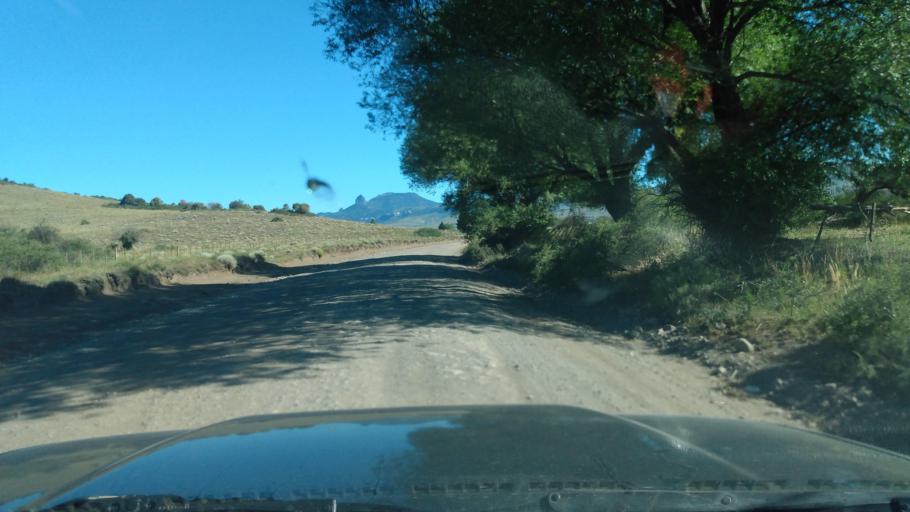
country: AR
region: Neuquen
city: Junin de los Andes
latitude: -39.8388
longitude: -71.1891
